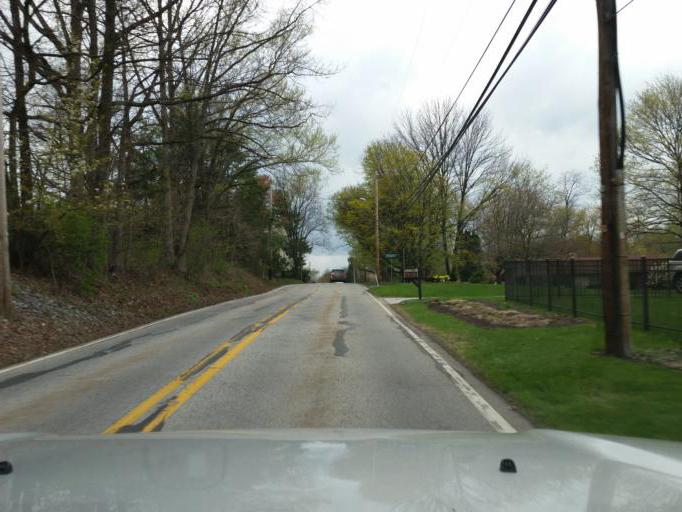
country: US
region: Pennsylvania
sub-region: Dauphin County
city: Paxtonia
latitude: 40.3102
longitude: -76.7744
